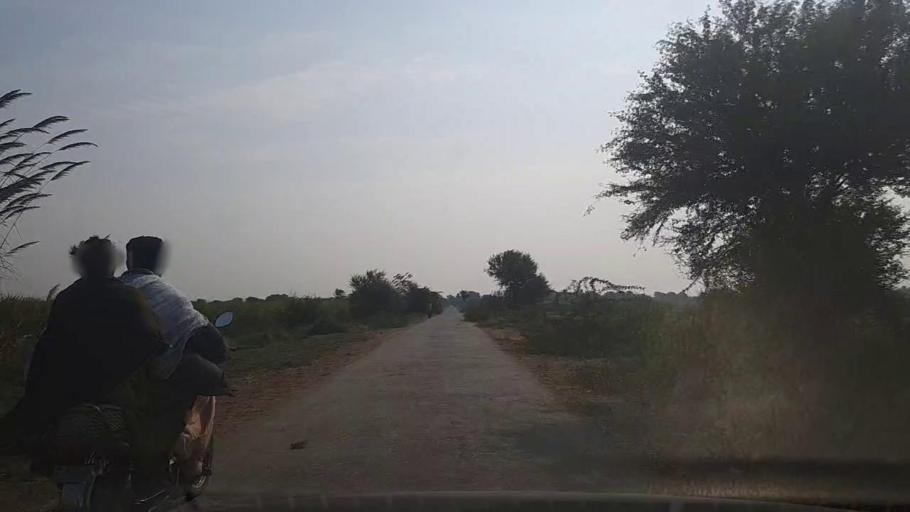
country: PK
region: Sindh
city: Bulri
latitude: 24.9721
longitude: 68.3268
